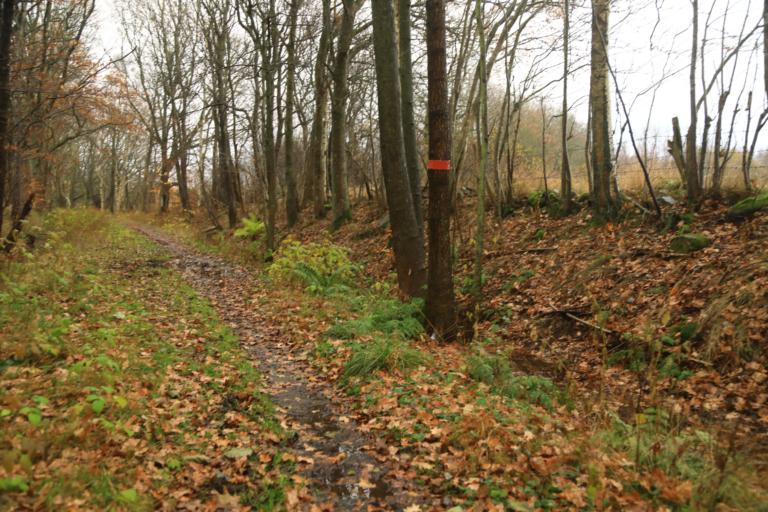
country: SE
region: Halland
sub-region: Varbergs Kommun
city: Traslovslage
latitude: 57.1159
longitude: 12.3052
